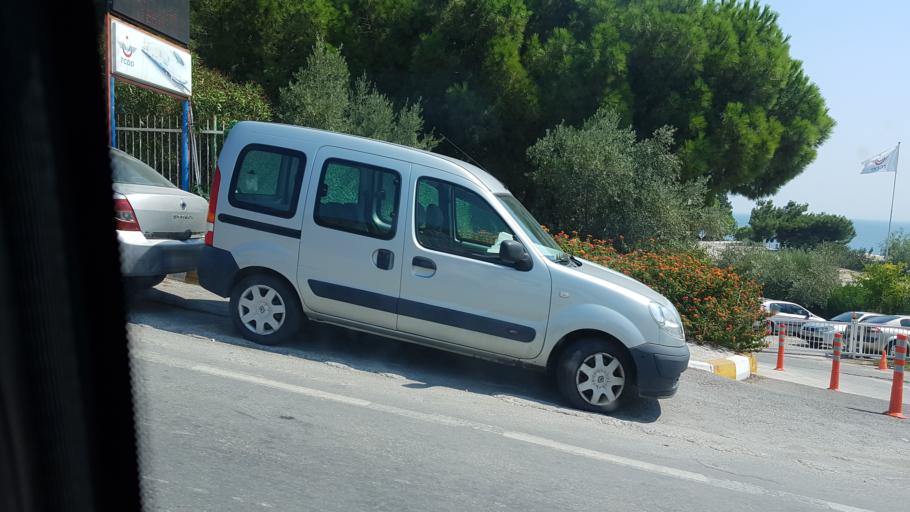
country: TR
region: Izmir
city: Urla
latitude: 38.3772
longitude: 26.7601
